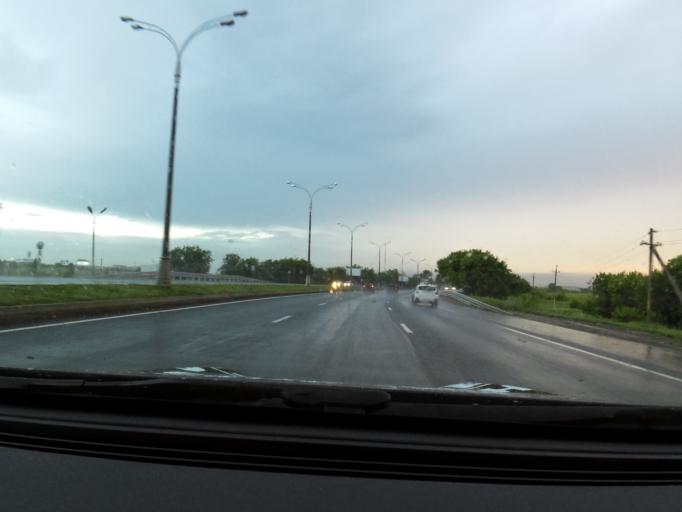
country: RU
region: Tatarstan
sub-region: Tukayevskiy Rayon
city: Naberezhnyye Chelny
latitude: 55.6689
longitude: 52.3190
